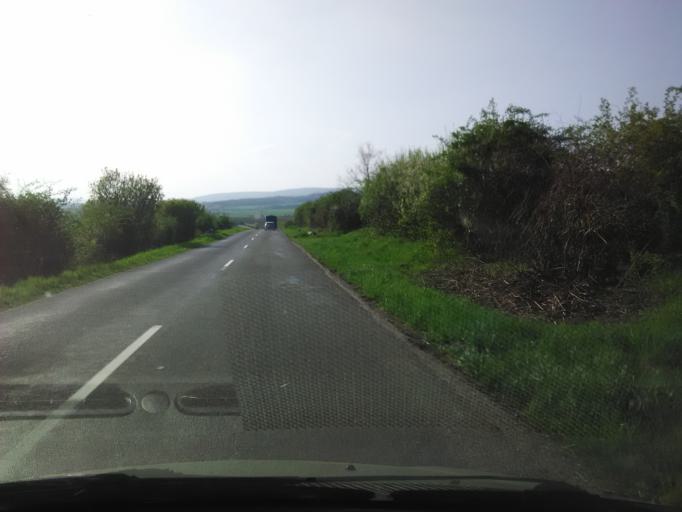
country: SK
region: Nitriansky
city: Levice
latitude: 48.2876
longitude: 18.6806
